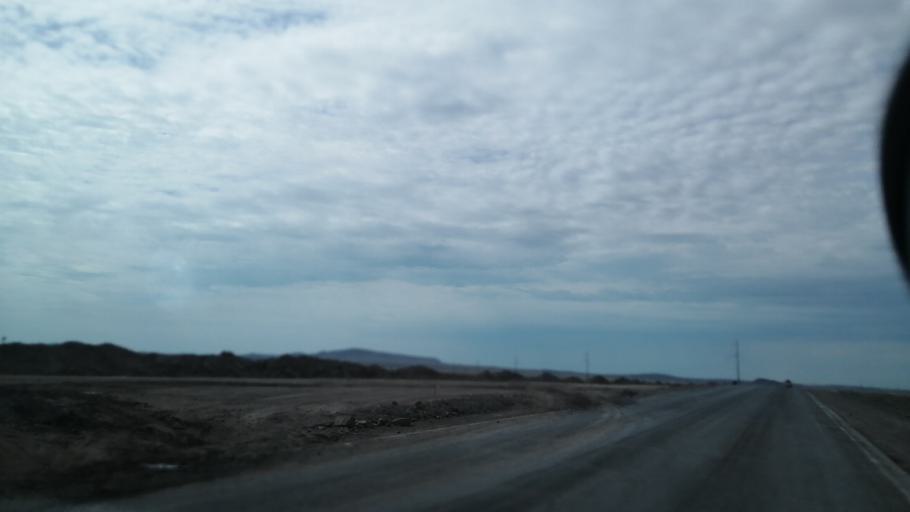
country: KZ
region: Qaraghandy
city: Balqash
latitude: 46.6849
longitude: 74.4300
